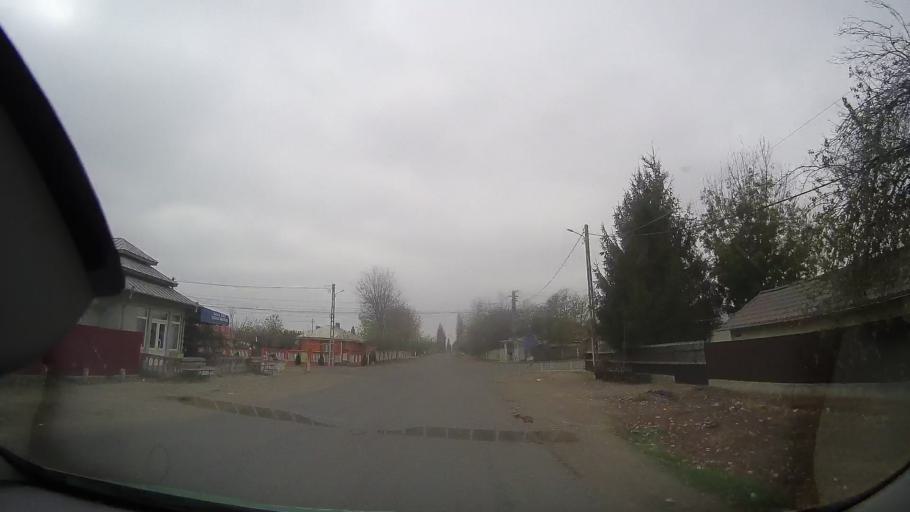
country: RO
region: Buzau
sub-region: Comuna Glodeanu-Silistea
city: Glodeanu-Silistea
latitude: 44.8215
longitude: 26.8333
